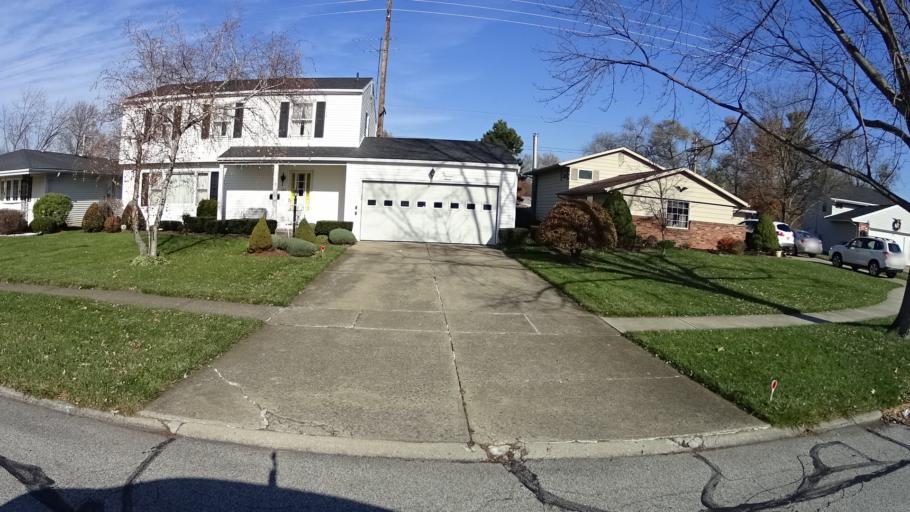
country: US
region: Ohio
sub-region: Lorain County
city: Sheffield
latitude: 41.4025
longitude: -82.0788
